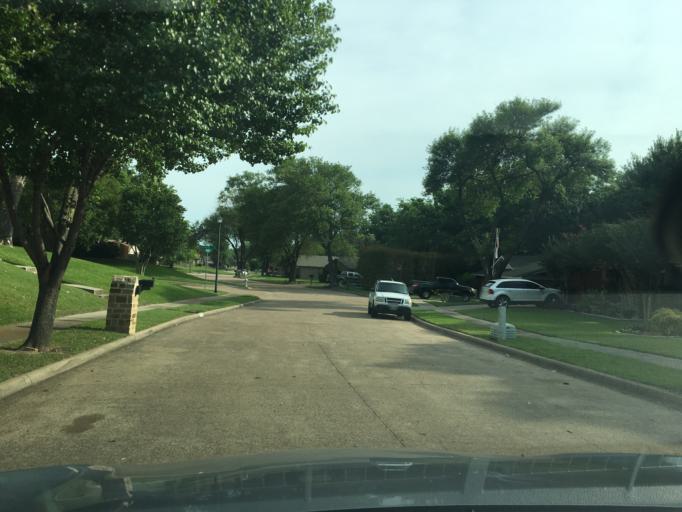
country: US
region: Texas
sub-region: Collin County
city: Plano
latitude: 32.9676
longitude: -96.6716
